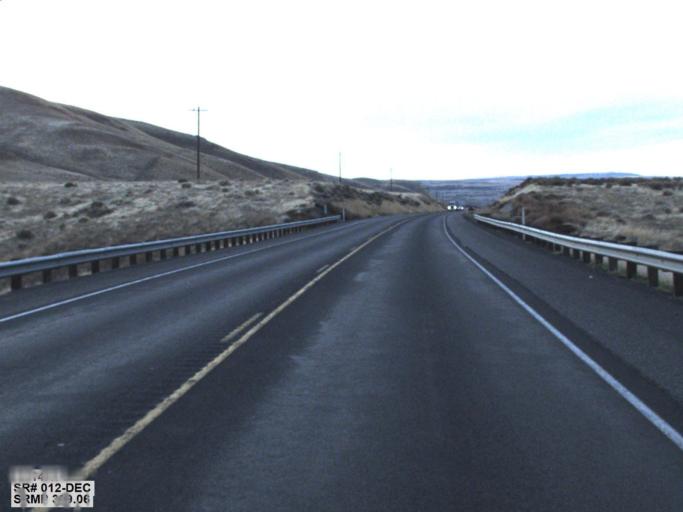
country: US
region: Washington
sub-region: Benton County
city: Finley
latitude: 46.0528
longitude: -118.8788
